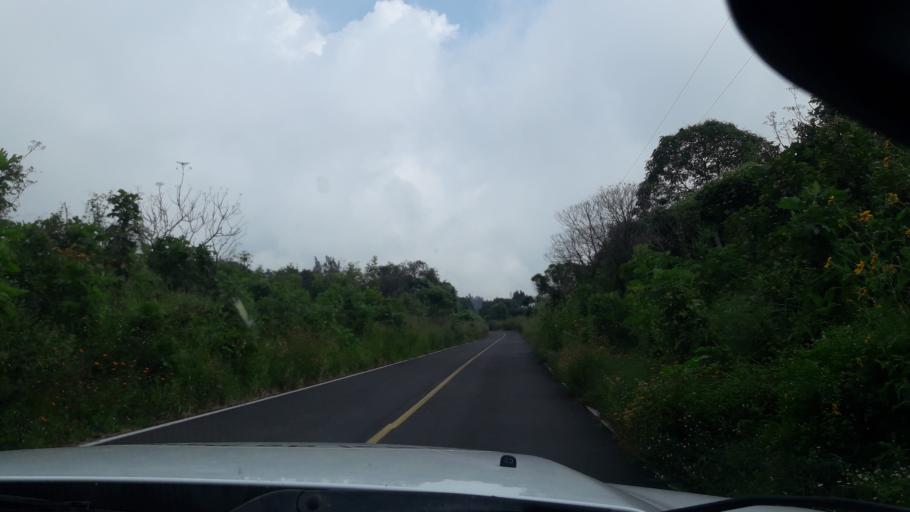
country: MX
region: Colima
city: Suchitlan
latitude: 19.4139
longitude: -103.6487
